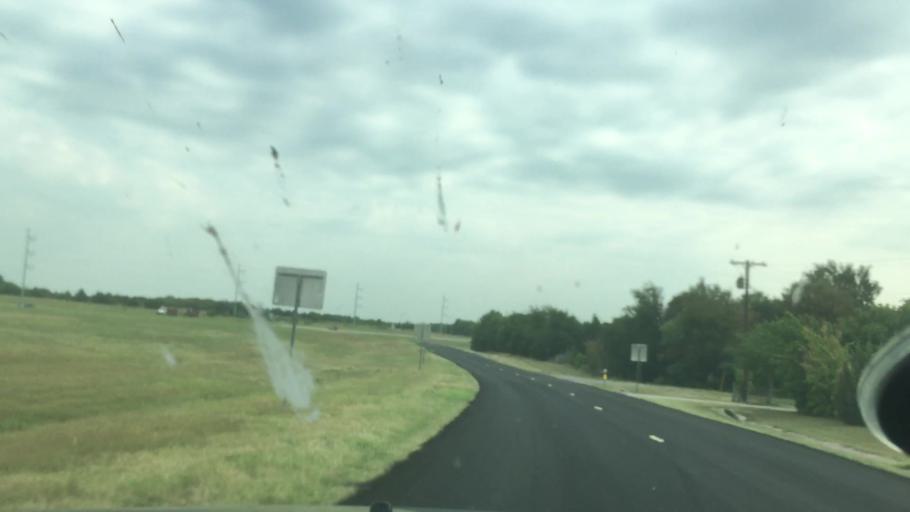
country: US
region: Texas
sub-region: Grayson County
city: Denison
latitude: 33.7788
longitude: -96.5825
